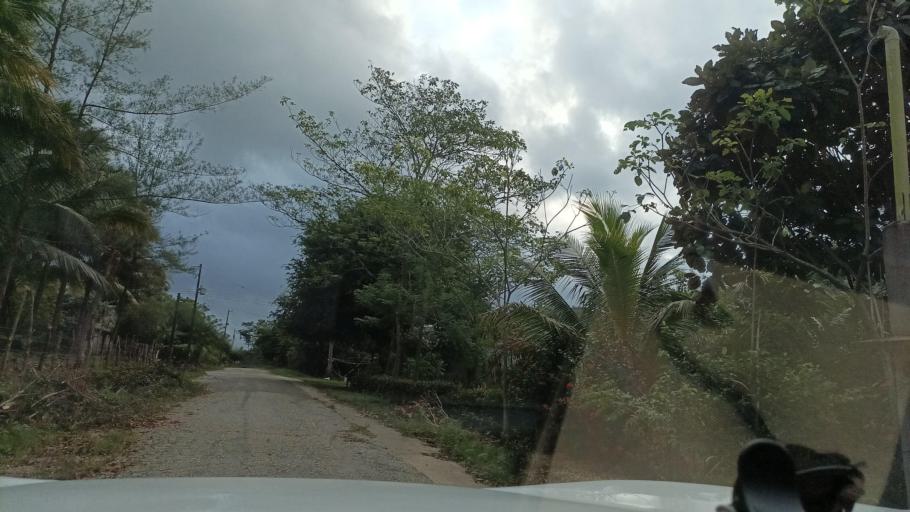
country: MX
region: Veracruz
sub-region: Moloacan
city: Cuichapa
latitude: 17.9215
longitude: -94.3680
